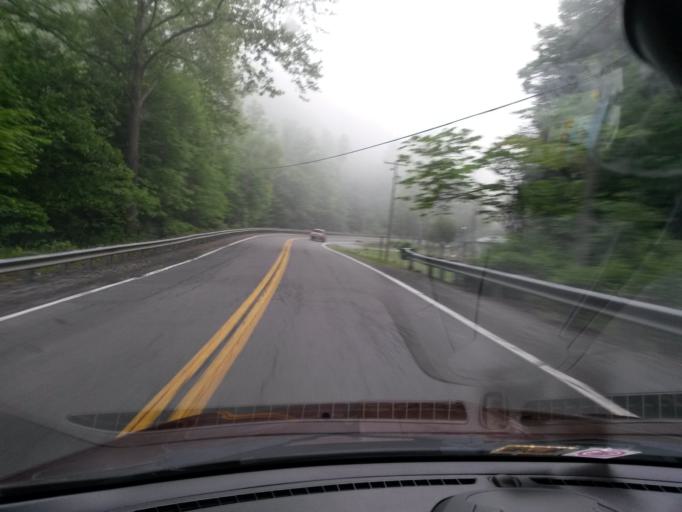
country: US
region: West Virginia
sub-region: Wyoming County
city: Pineville
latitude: 37.5034
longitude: -81.5432
